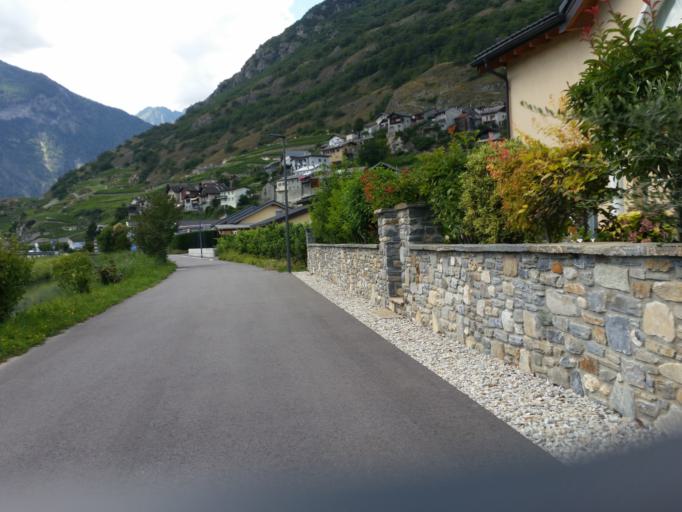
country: CH
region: Valais
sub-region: Martigny District
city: Fully
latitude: 46.1296
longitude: 7.0956
